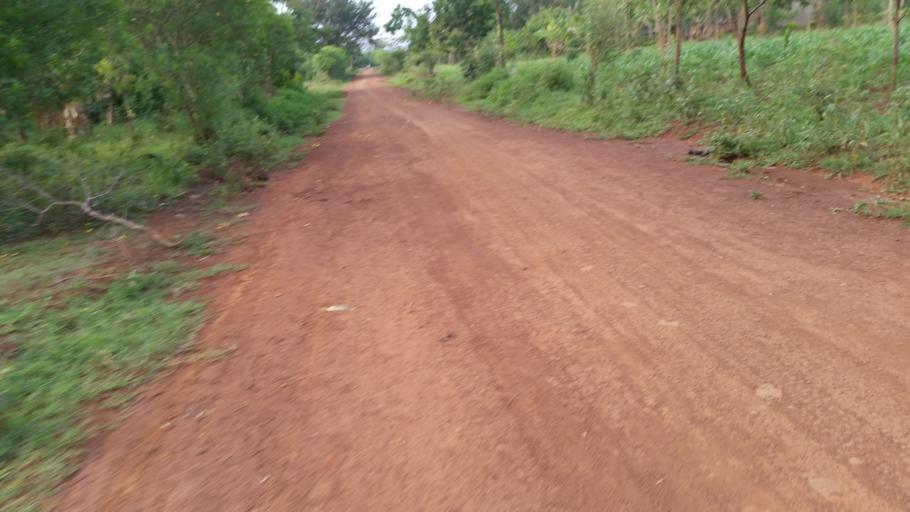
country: UG
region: Eastern Region
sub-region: Busia District
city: Busia
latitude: 0.5307
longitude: 34.0428
